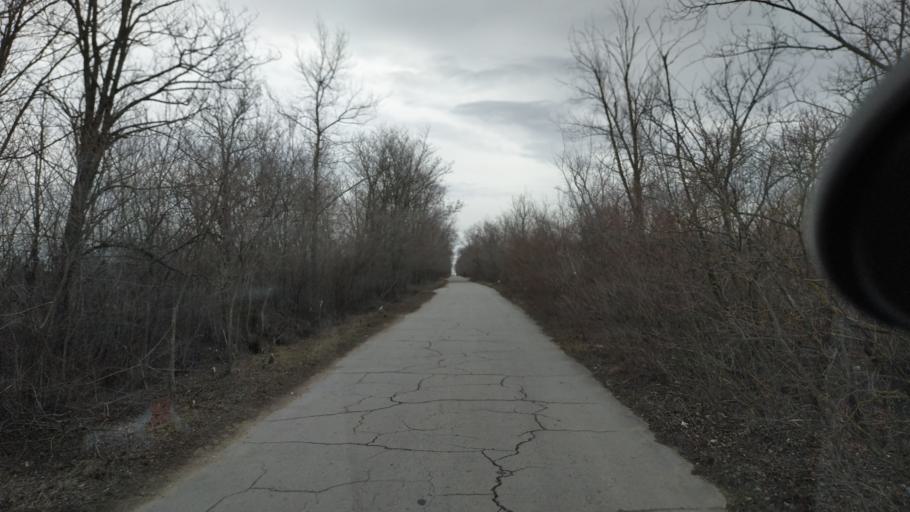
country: MD
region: Telenesti
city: Cocieri
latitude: 47.3296
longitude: 29.0903
